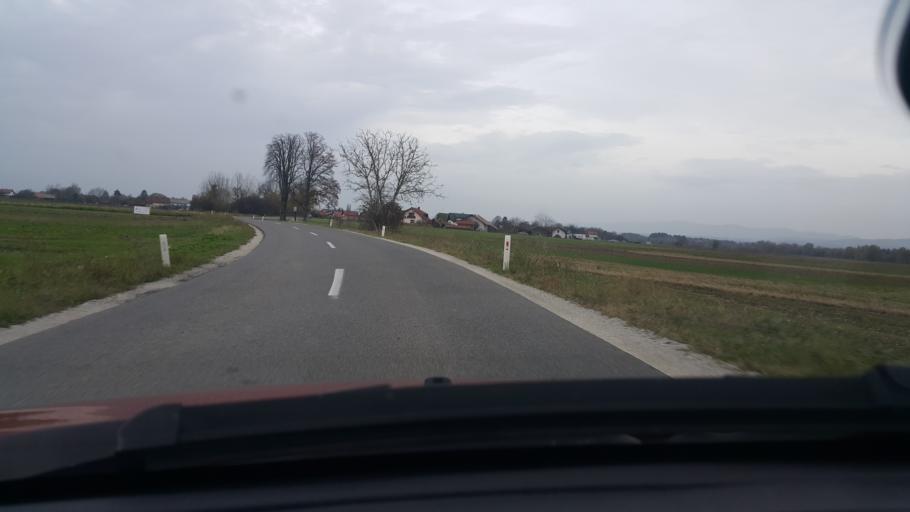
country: SI
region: Brezice
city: Brezice
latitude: 45.8970
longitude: 15.6377
